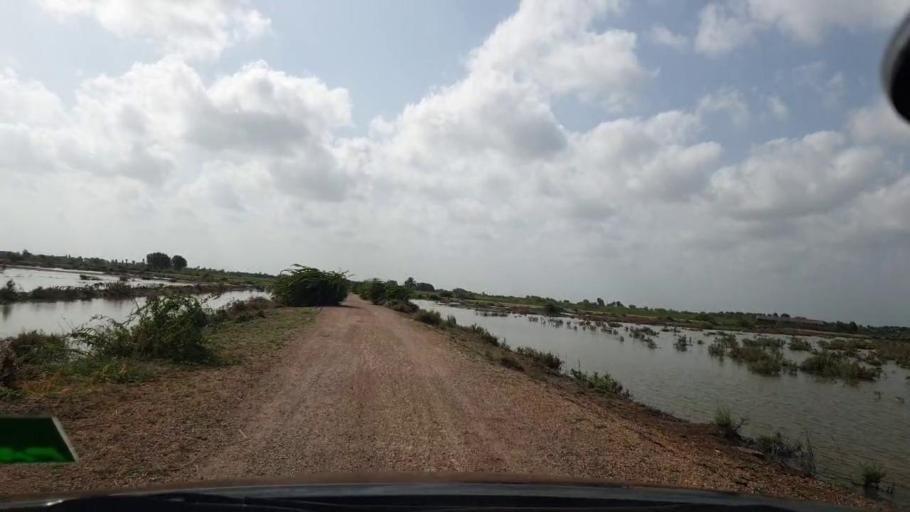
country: PK
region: Sindh
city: Kadhan
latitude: 24.6351
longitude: 69.0891
